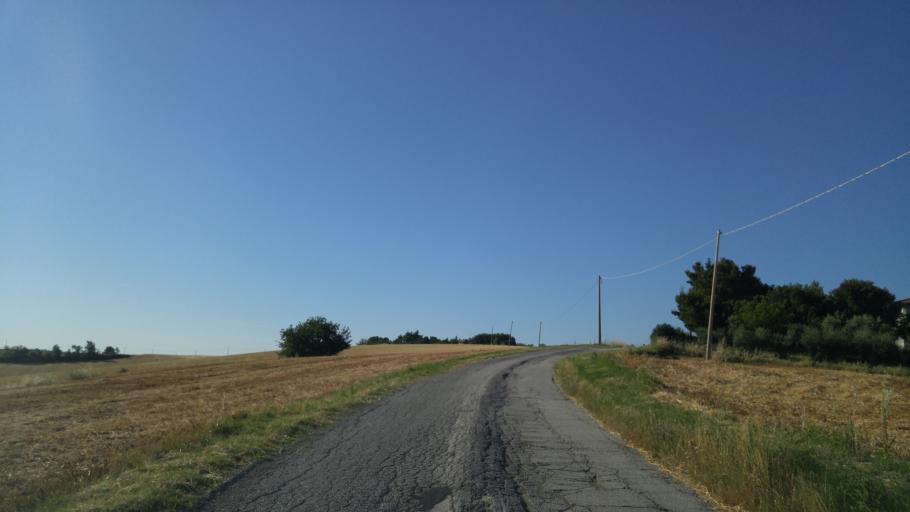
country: IT
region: The Marches
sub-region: Provincia di Pesaro e Urbino
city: Cartoceto
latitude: 43.7939
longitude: 12.8852
